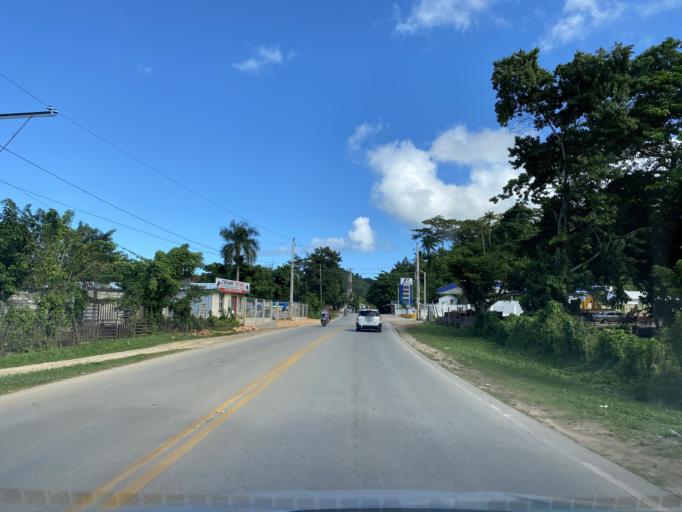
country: DO
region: Samana
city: Las Terrenas
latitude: 19.3046
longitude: -69.5453
